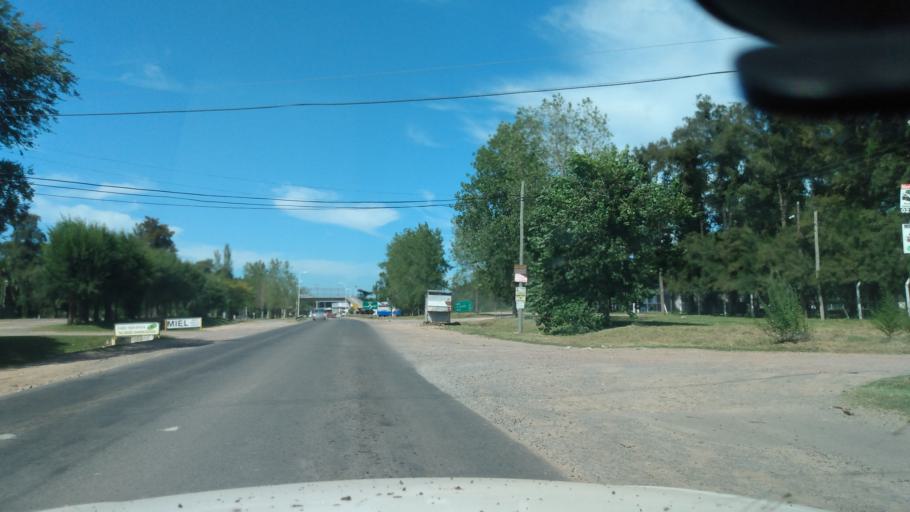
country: AR
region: Buenos Aires
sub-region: Partido de Lujan
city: Lujan
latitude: -34.5483
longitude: -59.1245
